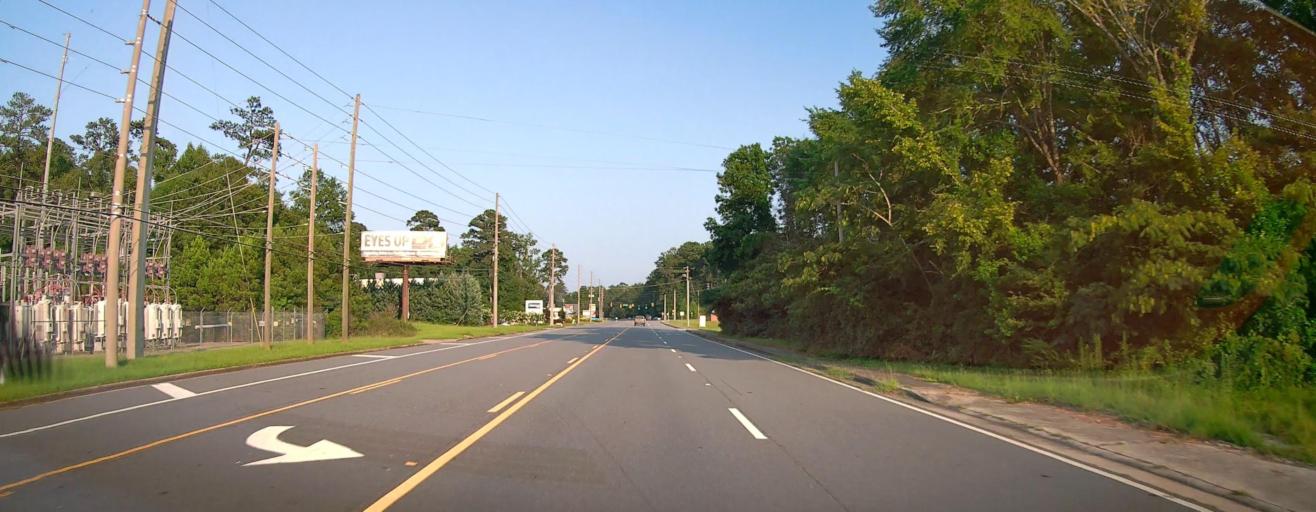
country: US
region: Georgia
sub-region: Bibb County
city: Macon
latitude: 32.8818
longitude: -83.7273
